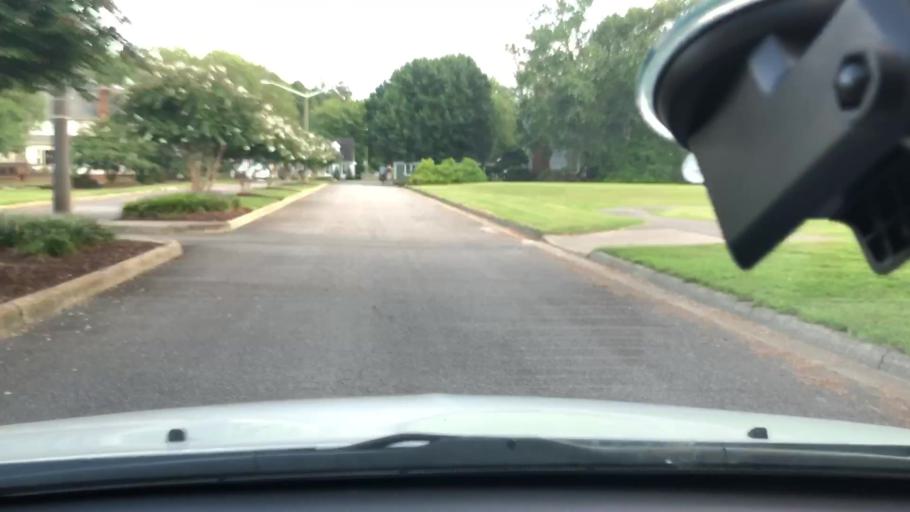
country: US
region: Virginia
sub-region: City of Chesapeake
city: Chesapeake
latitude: 36.7074
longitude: -76.2822
